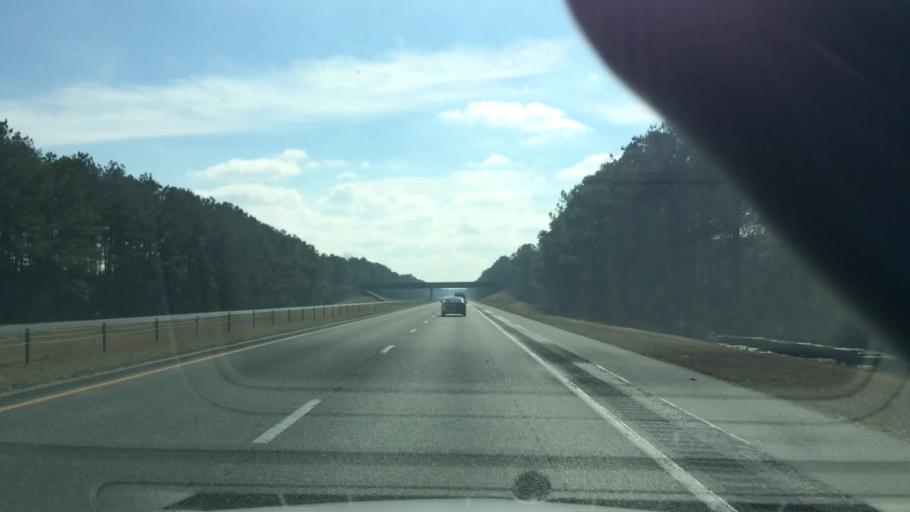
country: US
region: North Carolina
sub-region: Duplin County
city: Wallace
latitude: 34.7352
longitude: -77.9448
